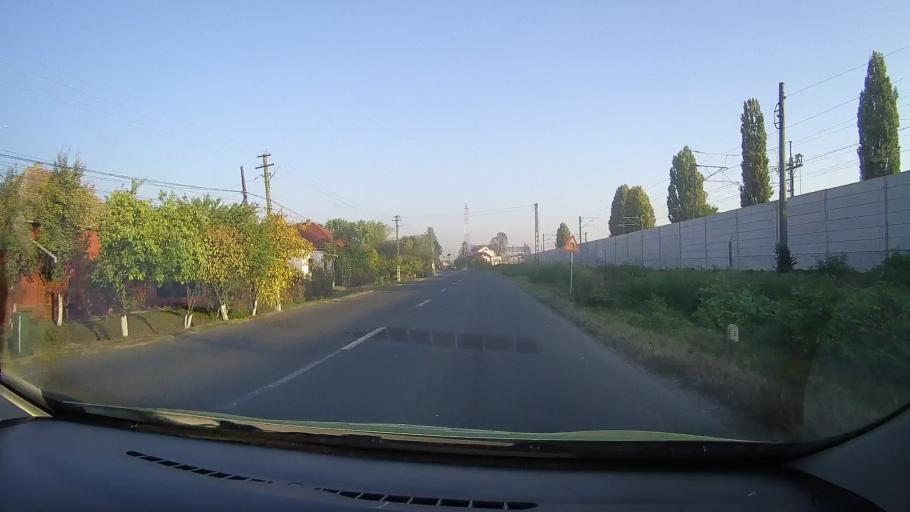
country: RO
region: Arad
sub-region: Comuna Sofronea
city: Sofronea
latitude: 46.2749
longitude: 21.3147
